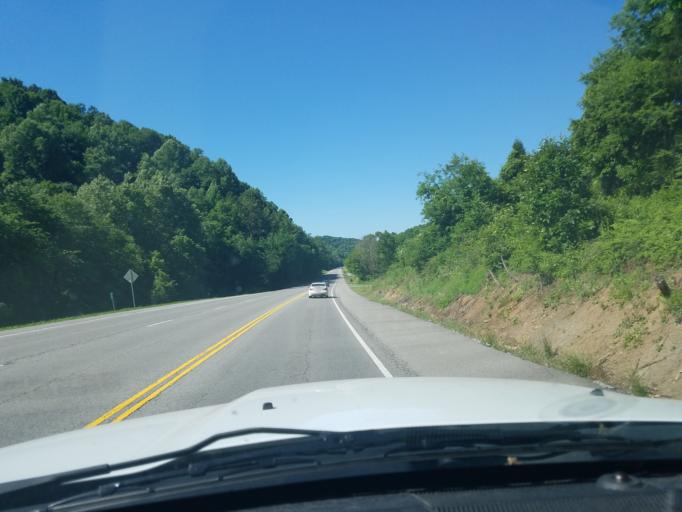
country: US
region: Tennessee
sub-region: Sumner County
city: Westmoreland
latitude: 36.5355
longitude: -86.2452
